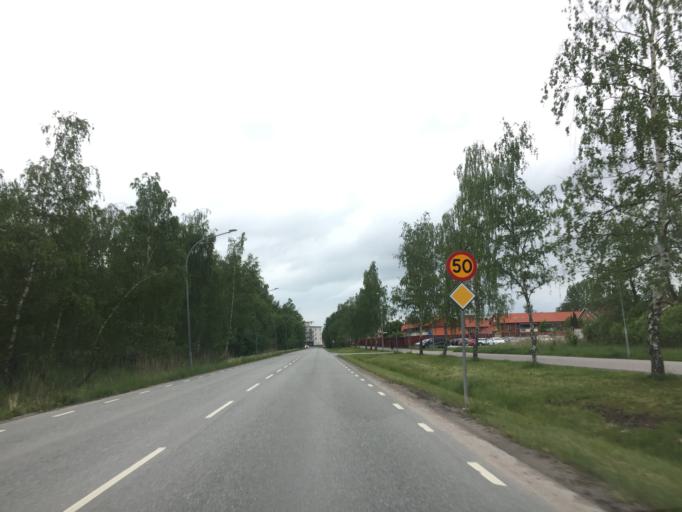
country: SE
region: OErebro
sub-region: Orebro Kommun
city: Orebro
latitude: 59.2516
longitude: 15.2297
